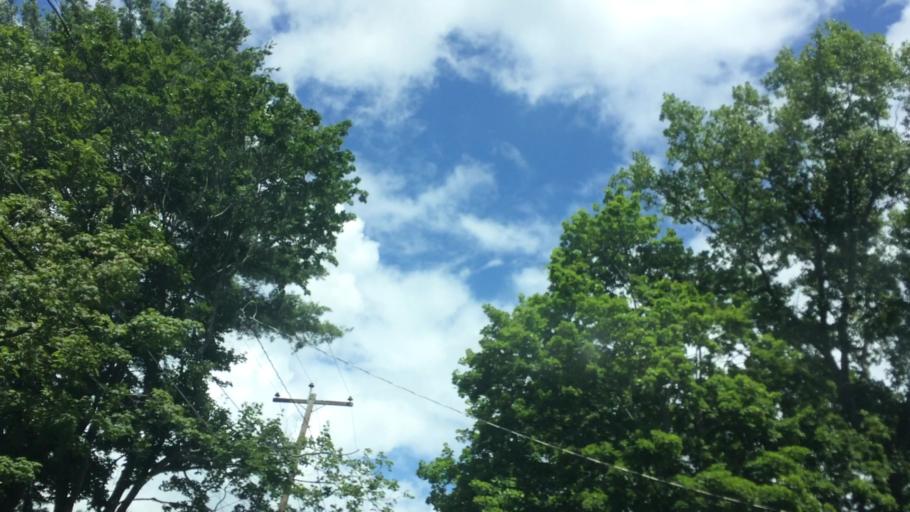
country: US
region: Massachusetts
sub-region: Middlesex County
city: Maynard
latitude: 42.4206
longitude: -71.4447
